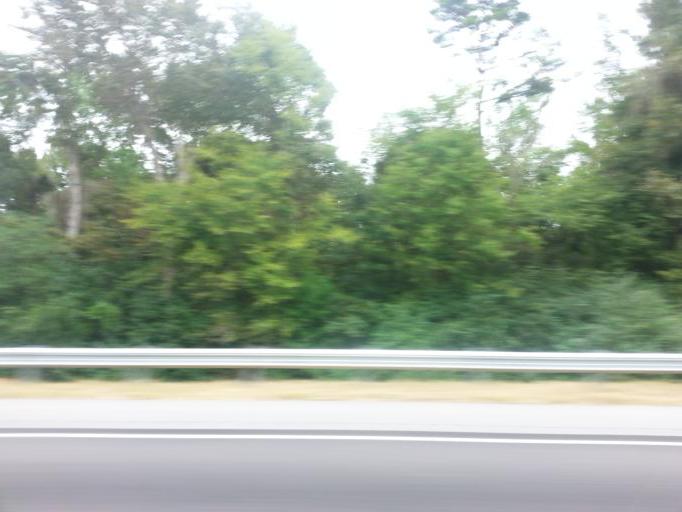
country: US
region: Alabama
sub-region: Conecuh County
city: Evergreen
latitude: 31.3914
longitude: -87.0301
